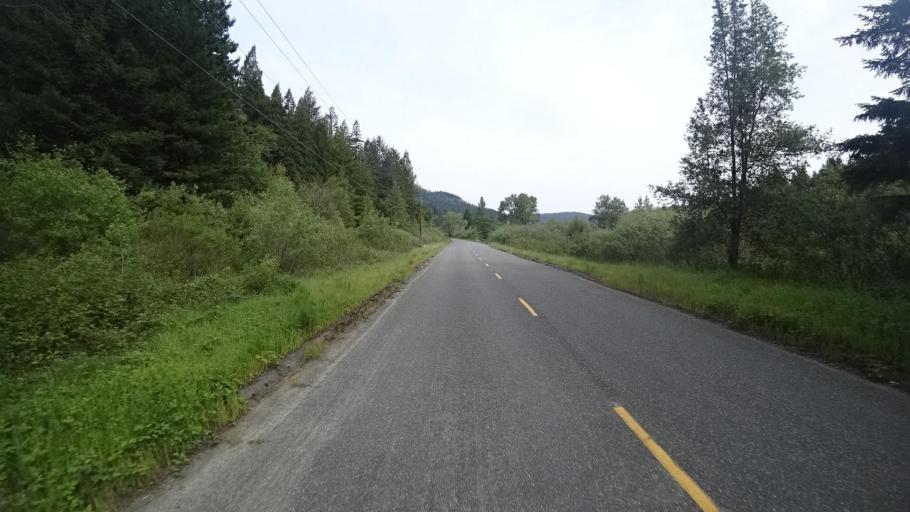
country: US
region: California
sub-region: Humboldt County
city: Redway
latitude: 40.2283
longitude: -123.8293
